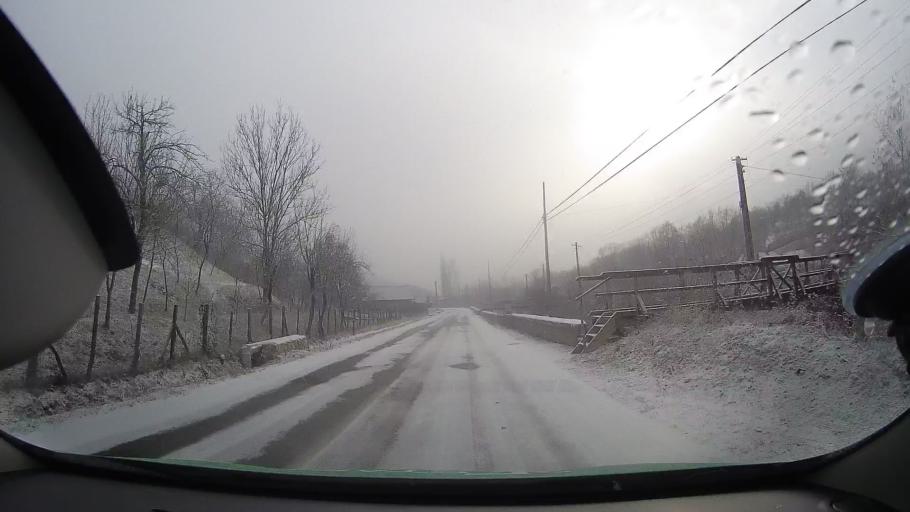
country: RO
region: Alba
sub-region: Comuna Livezile
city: Livezile
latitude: 46.3633
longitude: 23.6086
